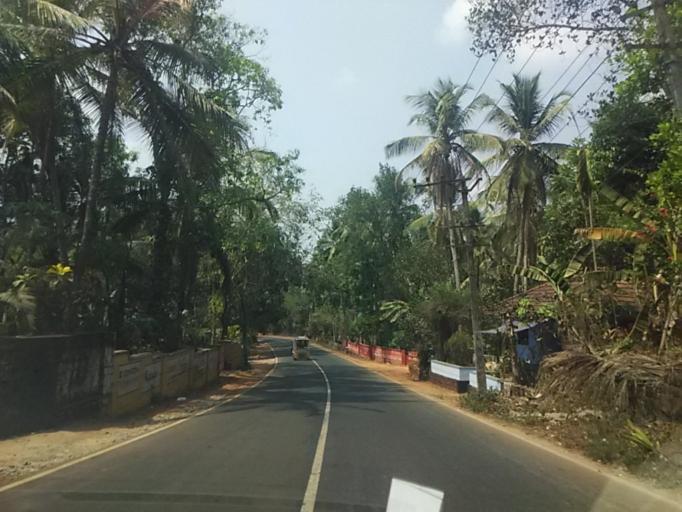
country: IN
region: Kerala
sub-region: Kozhikode
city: Naduvannur
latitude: 11.5060
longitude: 75.7744
